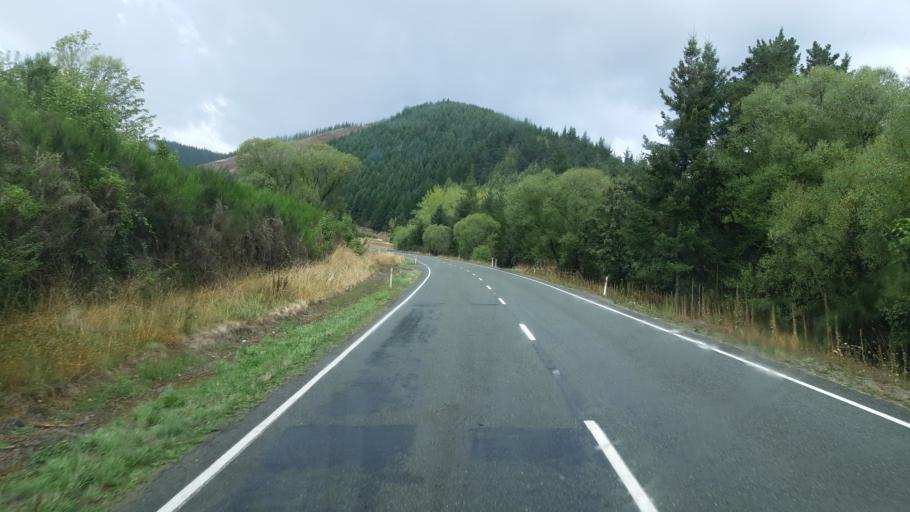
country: NZ
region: Tasman
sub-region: Tasman District
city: Wakefield
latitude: -41.4708
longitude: 172.8422
